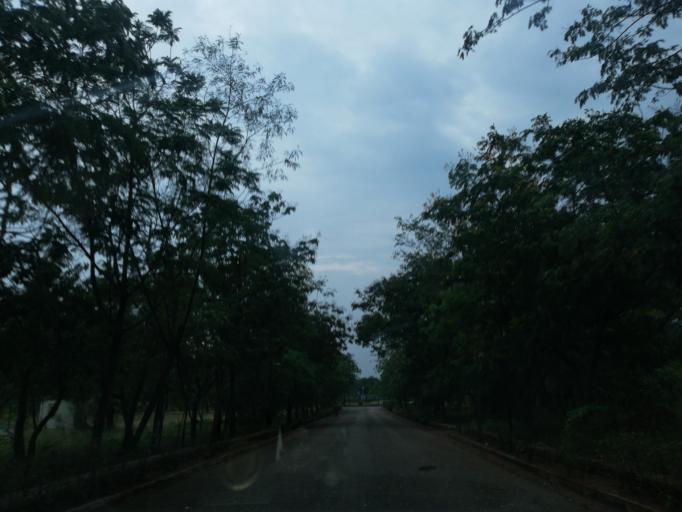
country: IN
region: Andhra Pradesh
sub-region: Guntur
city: Macherla
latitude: 16.6120
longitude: 79.2970
